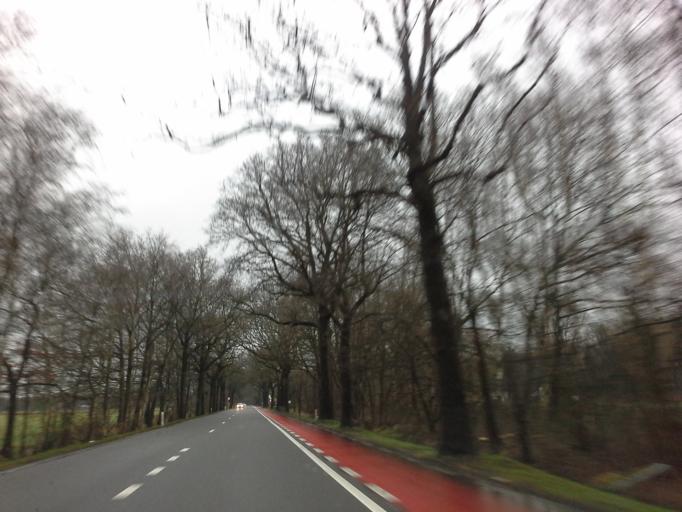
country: BE
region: Flanders
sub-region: Provincie Antwerpen
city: Turnhout
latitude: 51.3714
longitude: 4.9364
